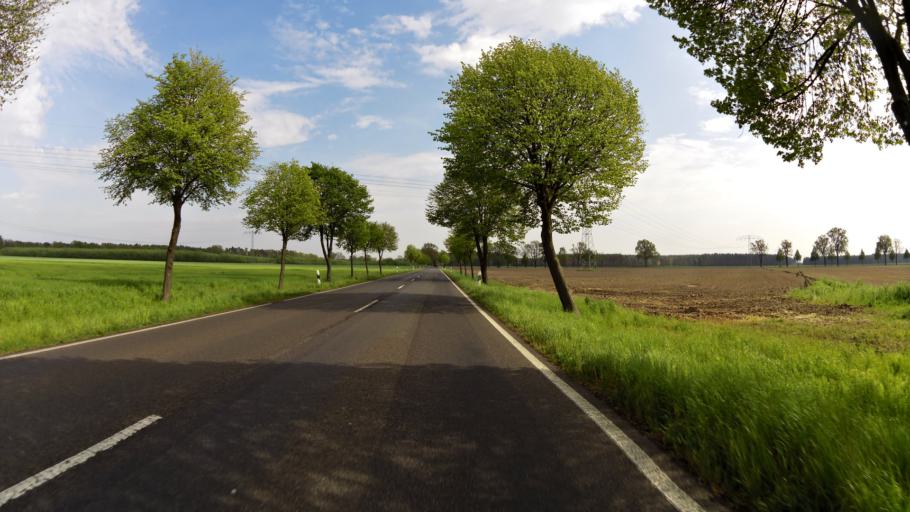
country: DE
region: Brandenburg
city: Storkow
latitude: 52.2762
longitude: 13.9109
